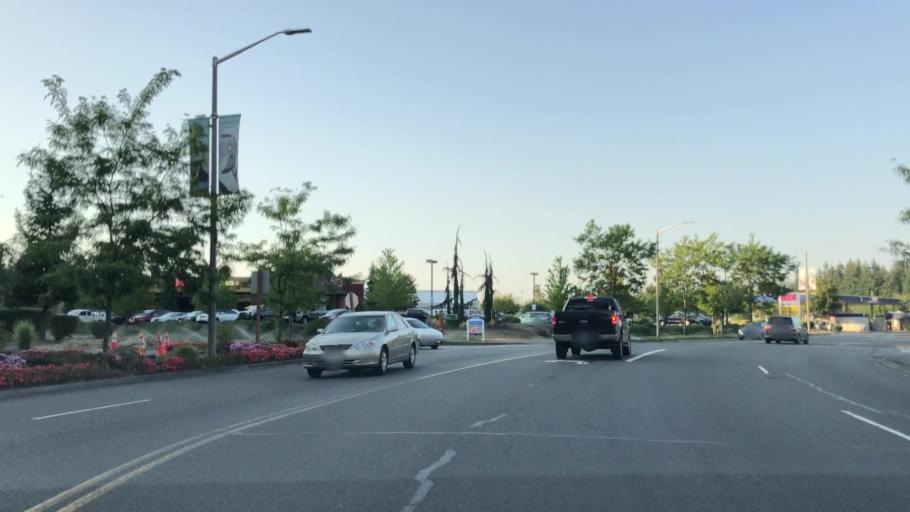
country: US
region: Washington
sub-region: Snohomish County
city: Marysville
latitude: 48.0765
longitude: -122.1880
